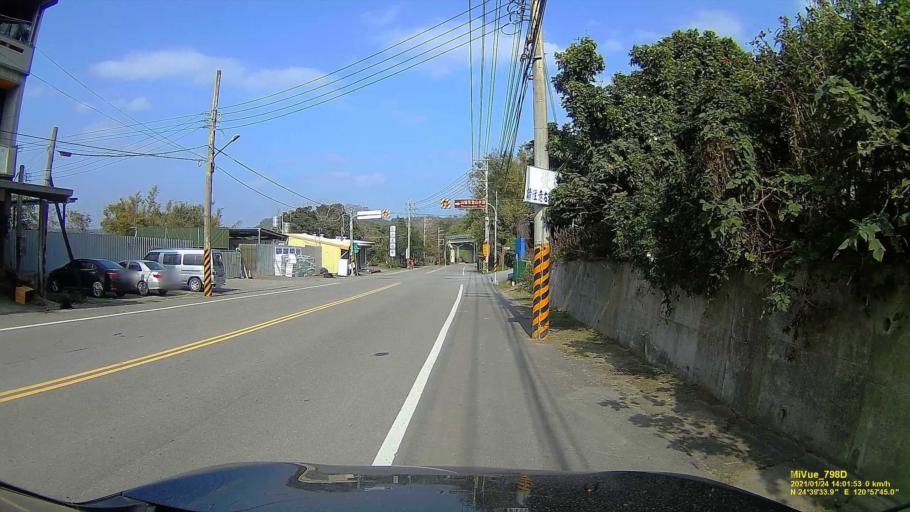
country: TW
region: Taiwan
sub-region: Hsinchu
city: Hsinchu
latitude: 24.6595
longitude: 120.9625
